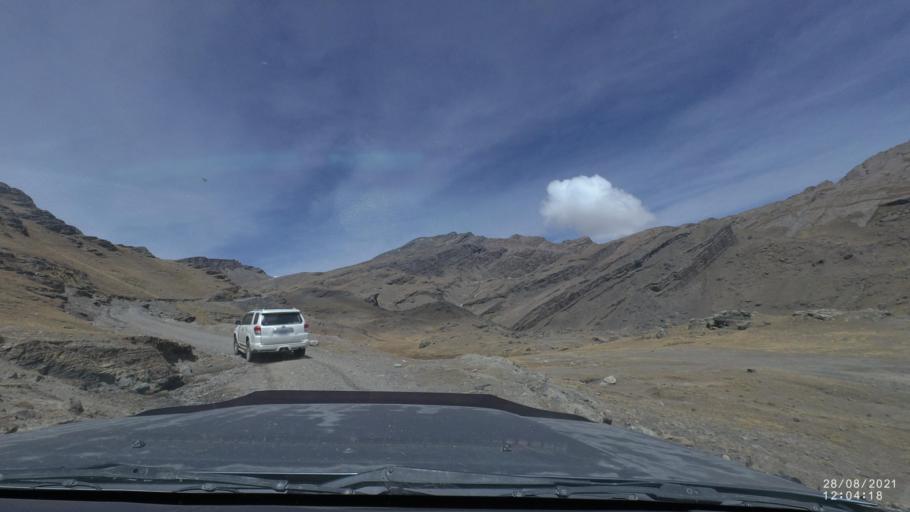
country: BO
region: Cochabamba
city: Sipe Sipe
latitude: -17.2663
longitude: -66.3845
